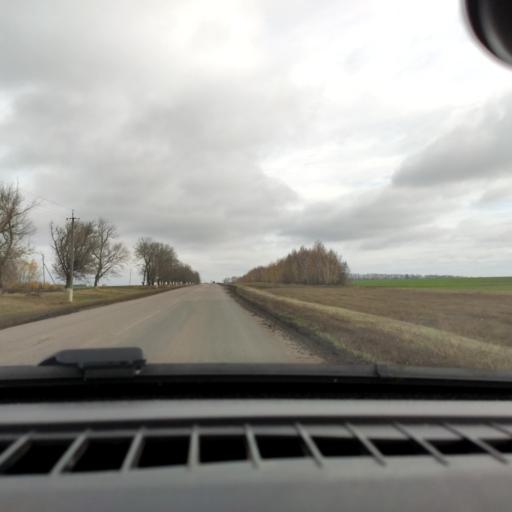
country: RU
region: Belgorod
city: Ilovka
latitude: 50.7127
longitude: 38.6619
